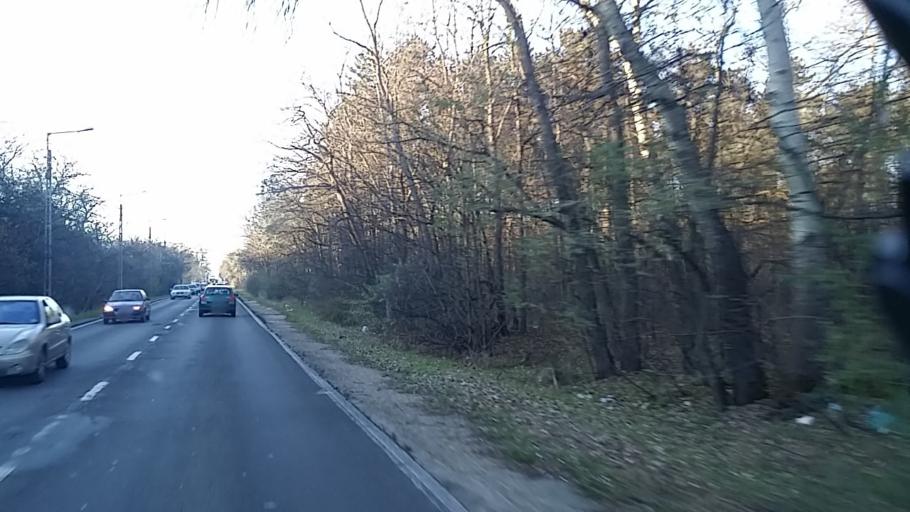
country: HU
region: Budapest
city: Budapest XVI. keruelet
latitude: 47.5387
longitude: 19.1574
